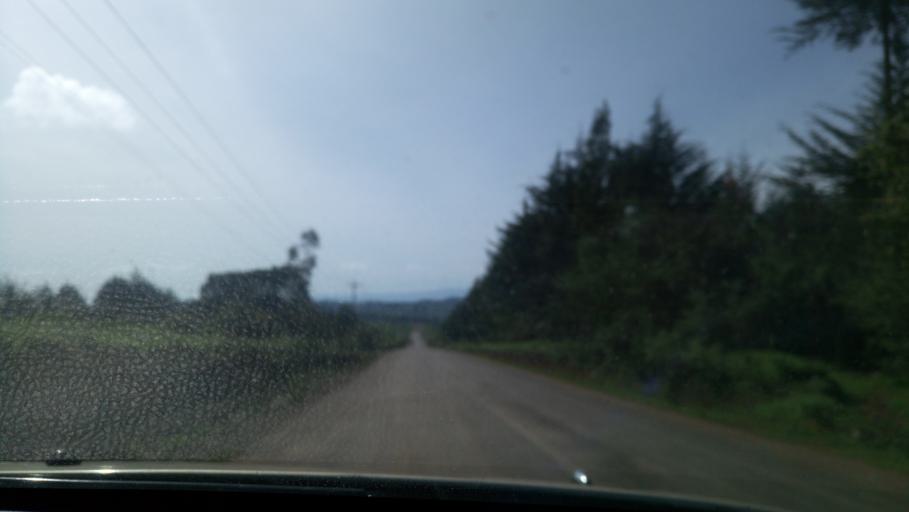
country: KE
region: Laikipia
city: Nyahururu
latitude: -0.1085
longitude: 36.2791
